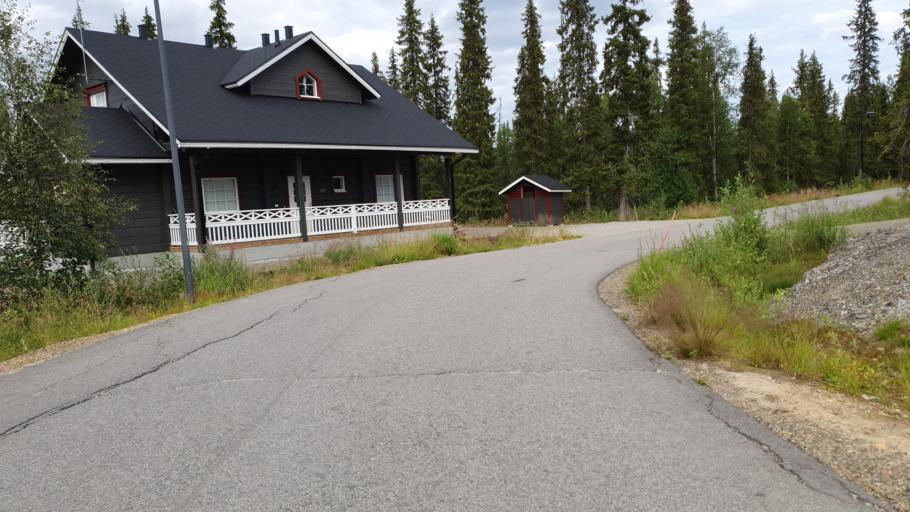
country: FI
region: Lapland
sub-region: Tunturi-Lappi
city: Kolari
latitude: 67.6019
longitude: 24.1439
